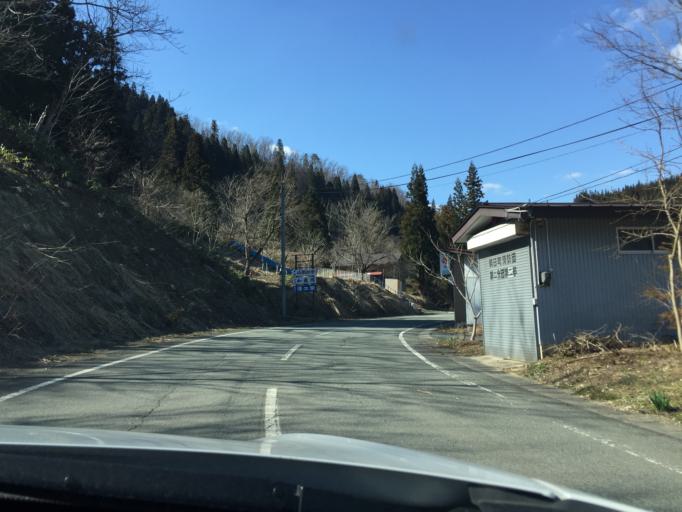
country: JP
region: Yamagata
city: Nagai
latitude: 38.2597
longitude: 140.1050
